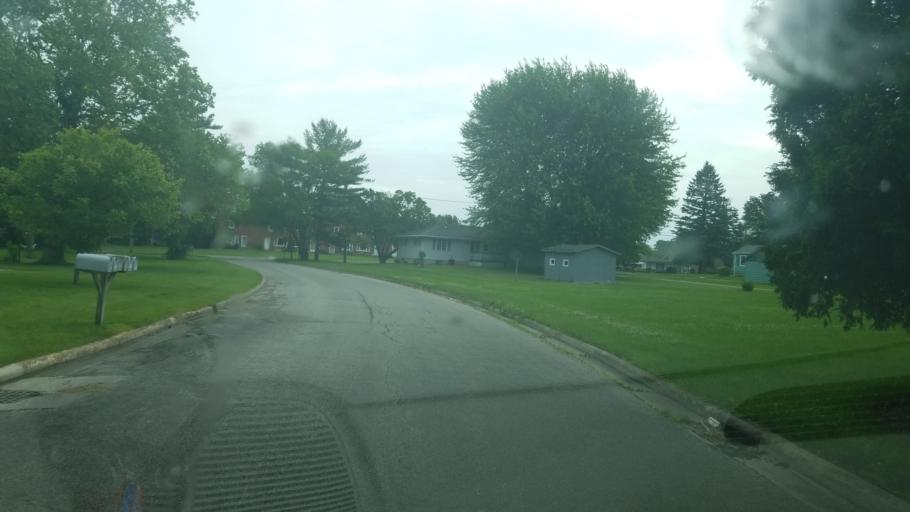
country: US
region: Ohio
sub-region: Crawford County
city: Bucyrus
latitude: 40.7892
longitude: -82.9823
